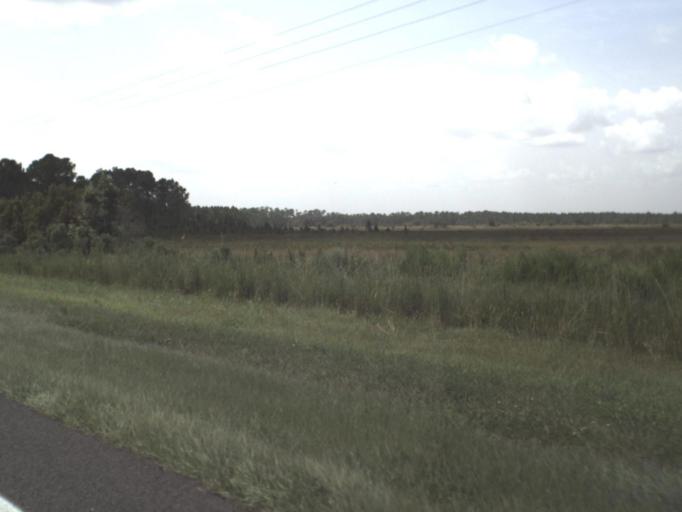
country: US
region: Florida
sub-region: Polk County
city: Crooked Lake Park
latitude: 27.7930
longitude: -81.5974
